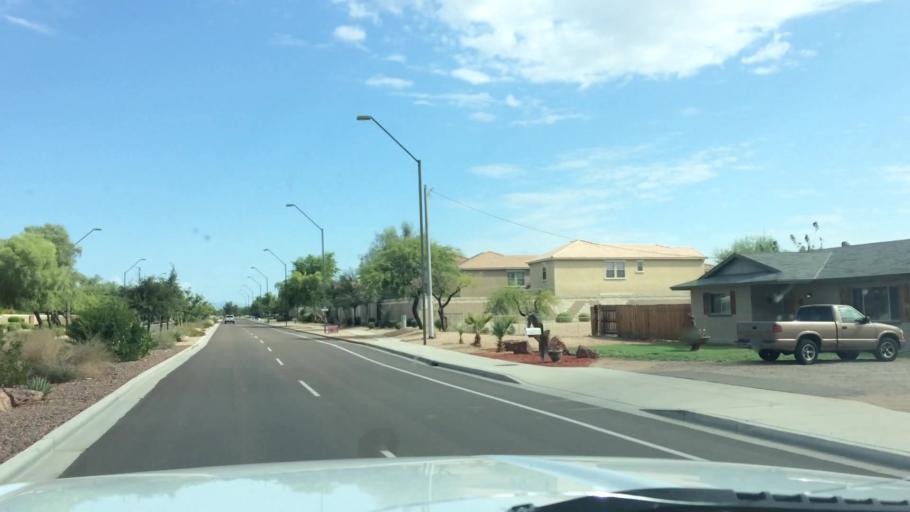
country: US
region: Arizona
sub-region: Maricopa County
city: Peoria
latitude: 33.5697
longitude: -112.2377
